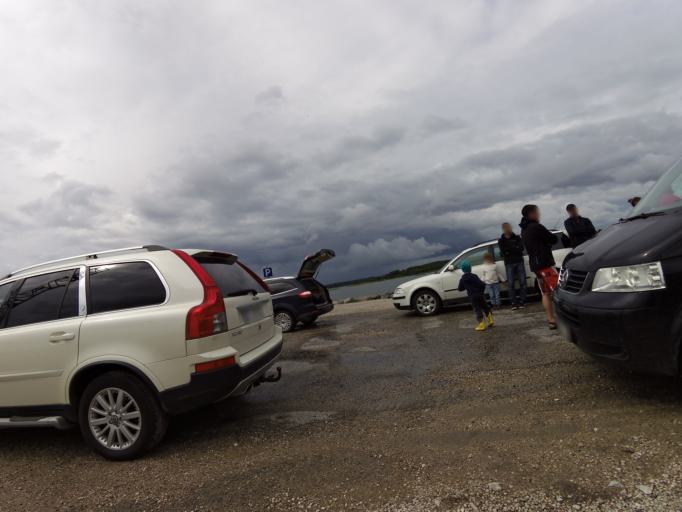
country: EE
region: Laeaene
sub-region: Vormsi vald
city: Hullo
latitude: 58.9710
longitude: 23.3128
